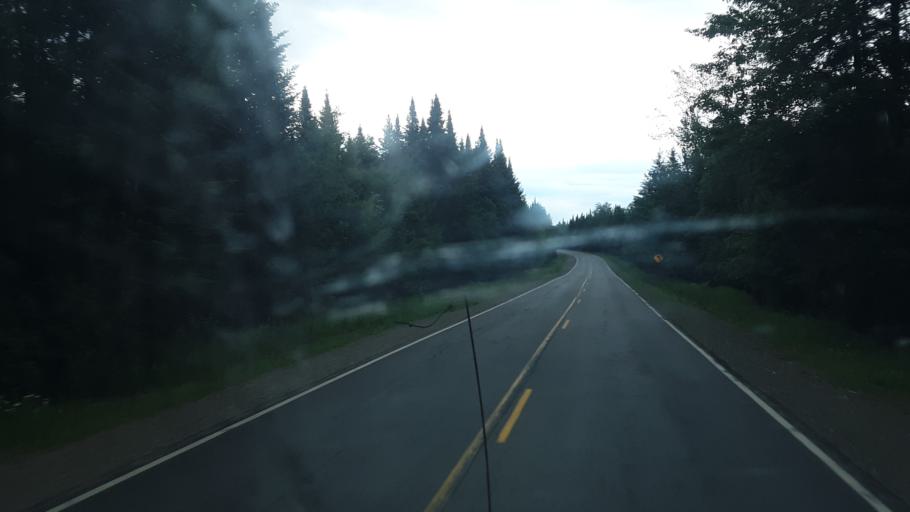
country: US
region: Maine
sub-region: Penobscot County
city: Medway
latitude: 45.6997
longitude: -68.2910
